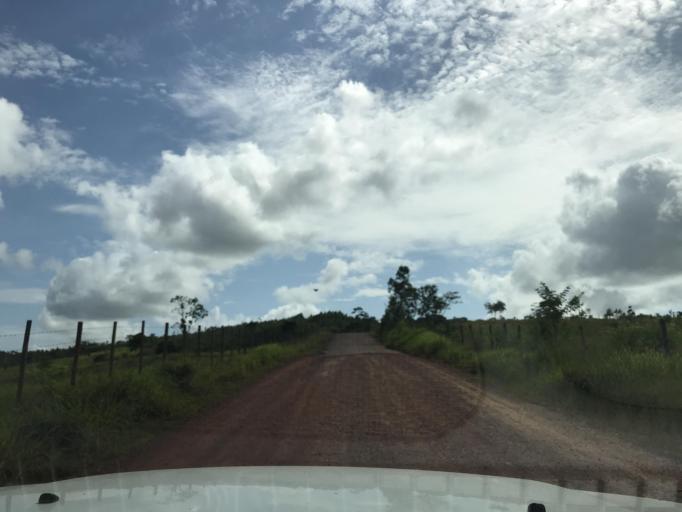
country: BR
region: Bahia
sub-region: Entre Rios
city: Entre Rios
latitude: -12.1745
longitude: -38.1153
